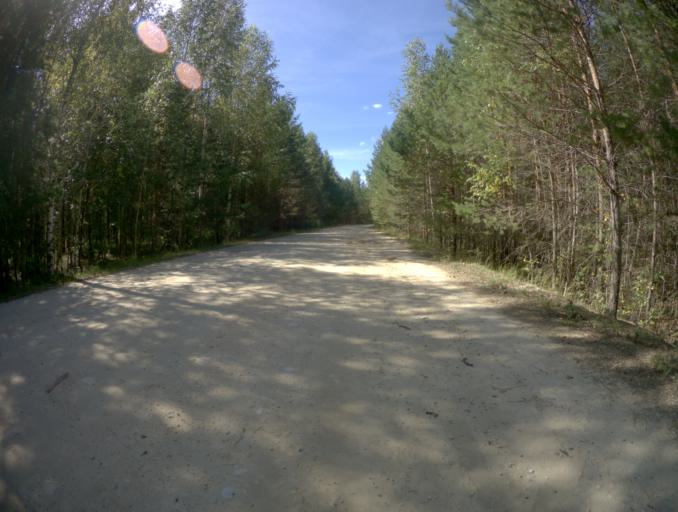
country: RU
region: Vladimir
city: Zolotkovo
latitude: 55.5925
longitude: 41.1614
